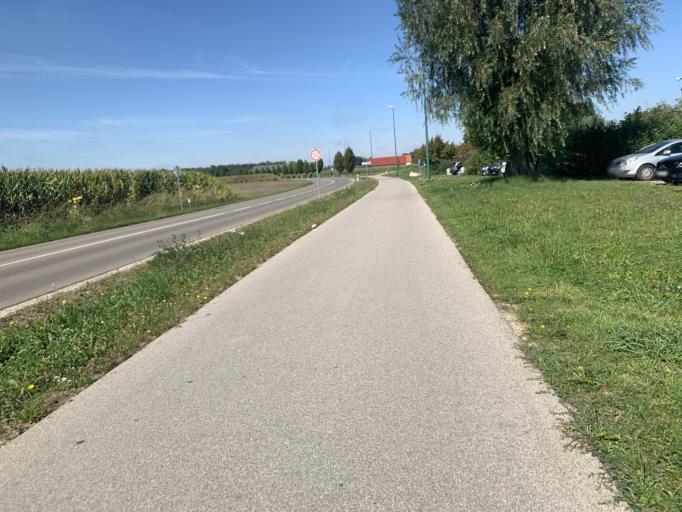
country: DE
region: Bavaria
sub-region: Swabia
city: Kissing
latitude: 48.3058
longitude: 10.9805
